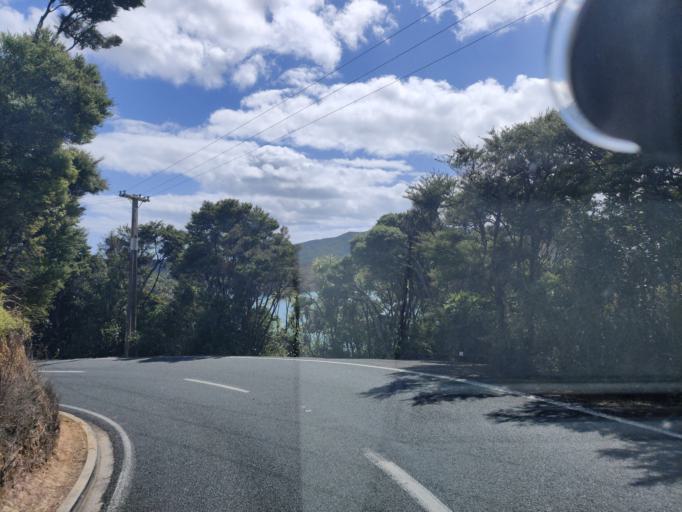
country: NZ
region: Northland
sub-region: Far North District
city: Paihia
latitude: -35.2576
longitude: 174.2454
